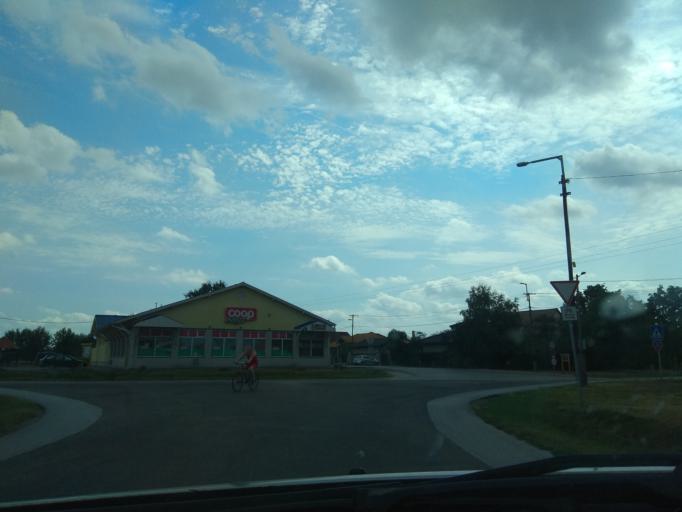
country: HU
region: Borsod-Abauj-Zemplen
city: Malyi
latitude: 48.0410
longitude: 20.8388
